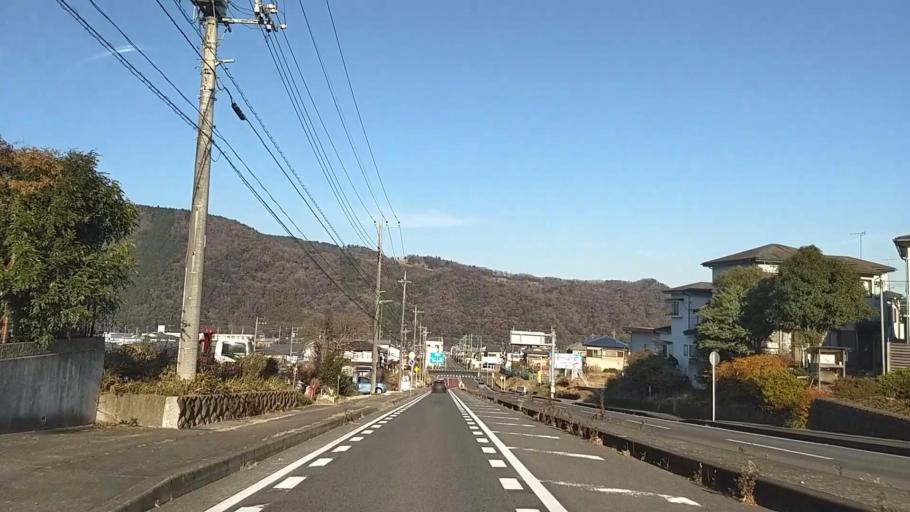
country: JP
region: Kanagawa
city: Zama
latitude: 35.5343
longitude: 139.2702
